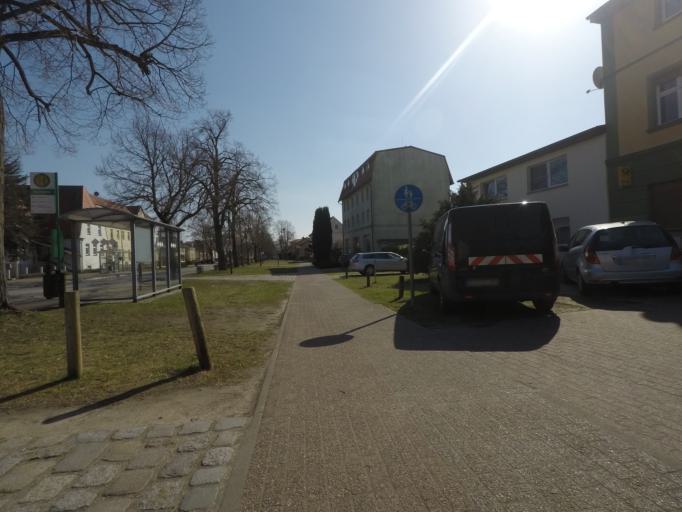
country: DE
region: Brandenburg
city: Britz
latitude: 52.8668
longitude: 13.7488
